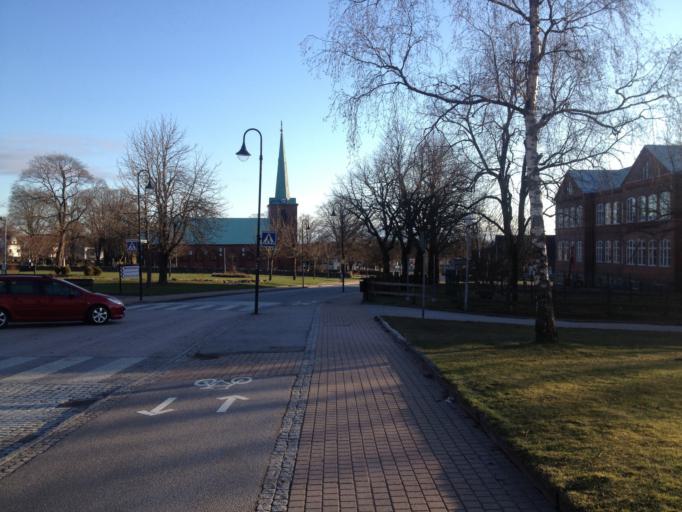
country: SE
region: Joenkoeping
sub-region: Gislaveds Kommun
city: Gislaved
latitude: 57.3040
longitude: 13.5387
